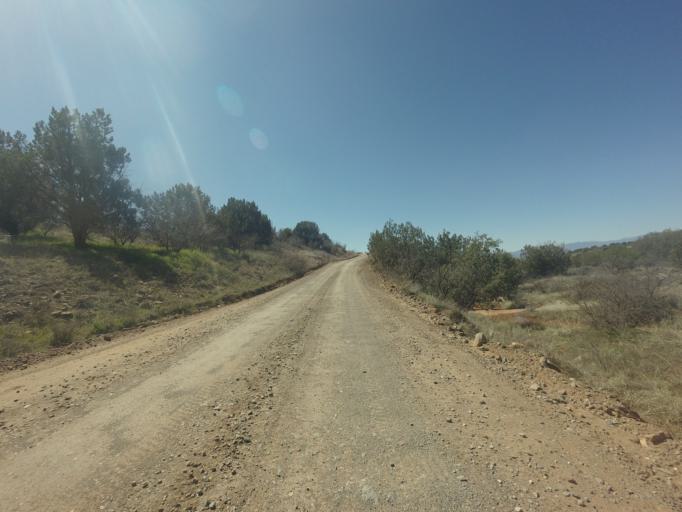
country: US
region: Arizona
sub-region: Yavapai County
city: Lake Montezuma
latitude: 34.6540
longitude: -111.7169
